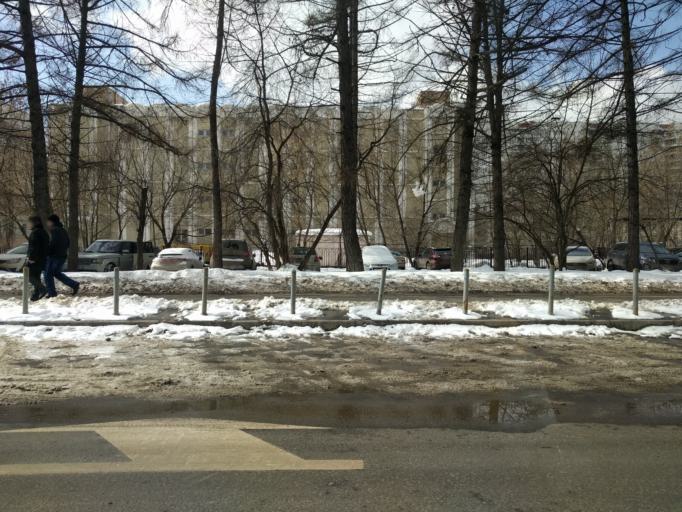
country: RU
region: Moskovskaya
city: Izmaylovo
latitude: 55.7979
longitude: 37.7992
